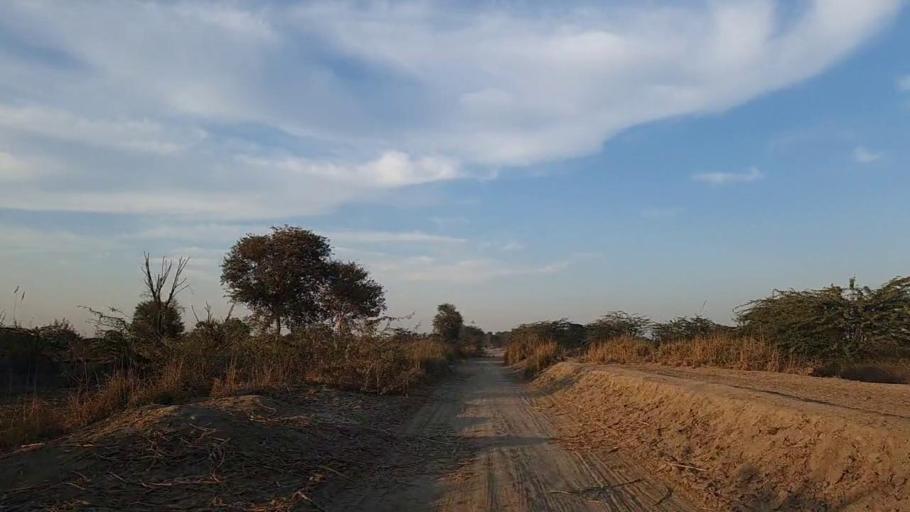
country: PK
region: Sindh
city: Bandhi
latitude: 26.6051
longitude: 68.3592
